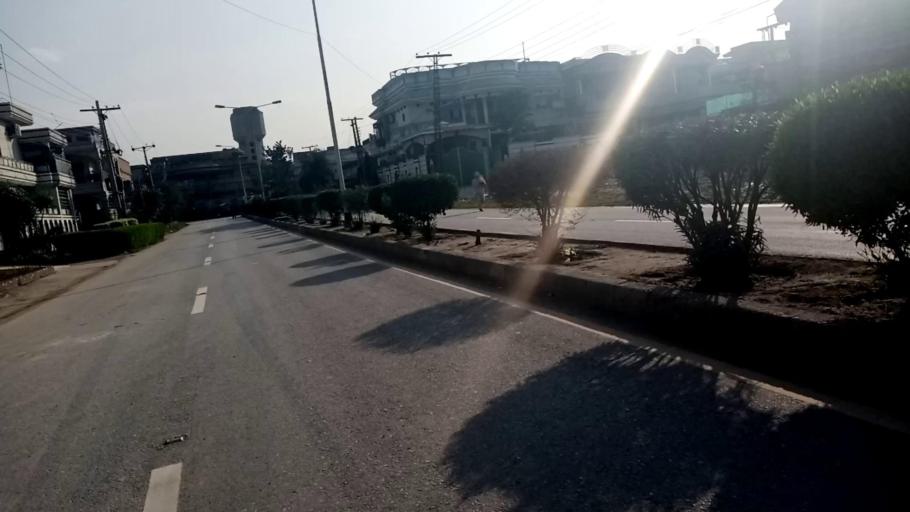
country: PK
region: Khyber Pakhtunkhwa
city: Peshawar
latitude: 33.9862
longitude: 71.4455
